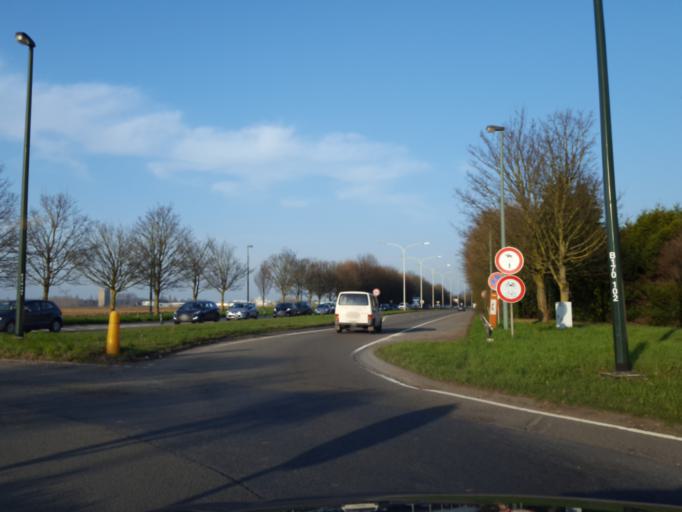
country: BE
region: Wallonia
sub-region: Province du Brabant Wallon
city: Nivelles
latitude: 50.5811
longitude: 4.3401
